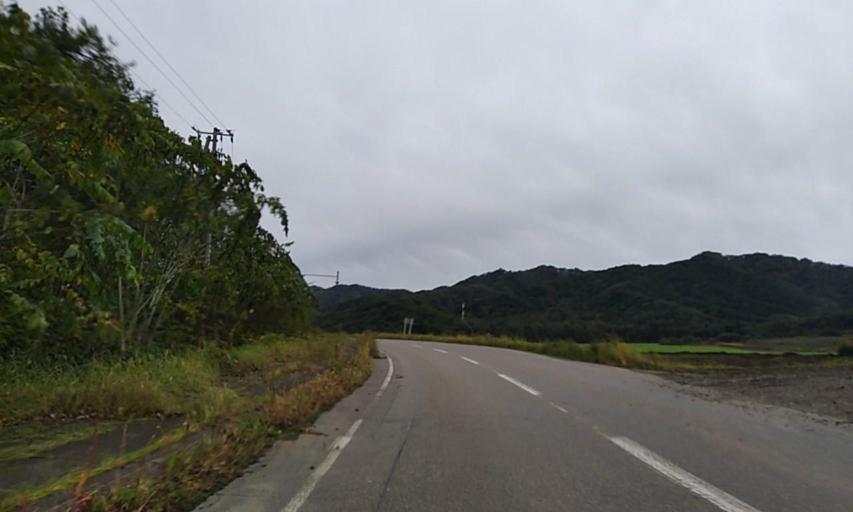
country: JP
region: Hokkaido
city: Obihiro
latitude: 42.6910
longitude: 143.0527
